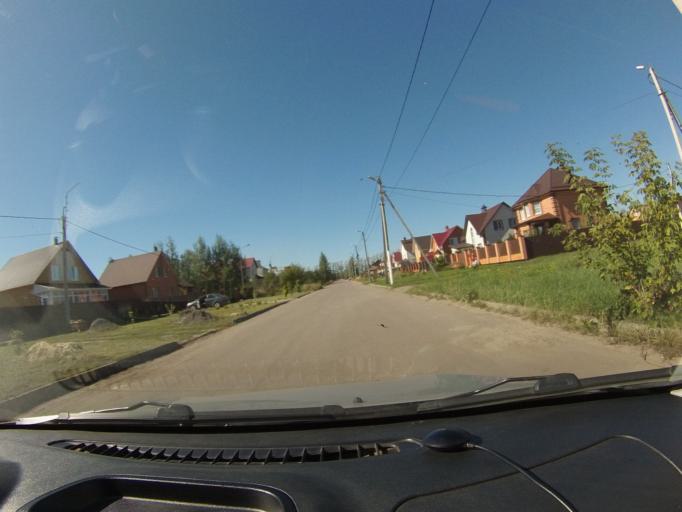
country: RU
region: Tambov
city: Tambov
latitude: 52.7688
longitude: 41.3739
